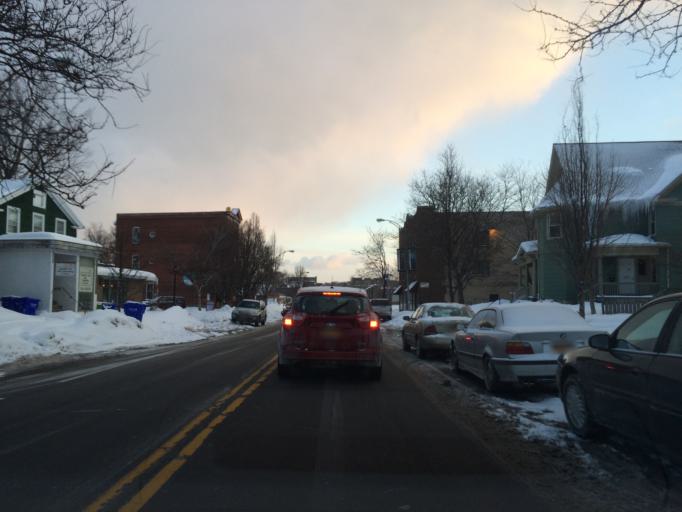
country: US
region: New York
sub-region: Monroe County
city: Rochester
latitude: 43.1459
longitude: -77.6054
